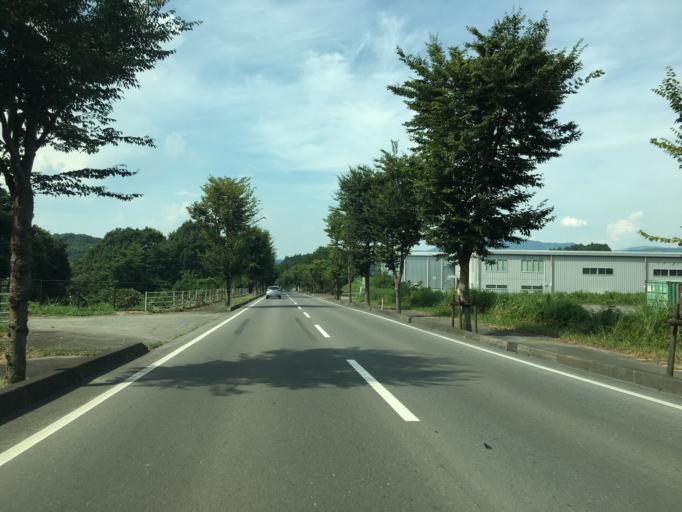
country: JP
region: Fukushima
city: Sukagawa
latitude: 37.2332
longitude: 140.4354
